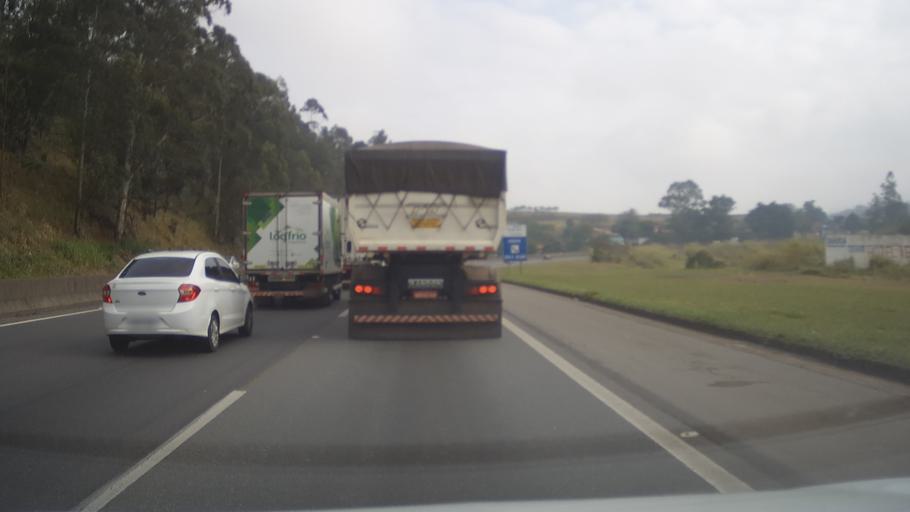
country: BR
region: Sao Paulo
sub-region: Atibaia
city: Atibaia
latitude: -23.0804
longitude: -46.5697
